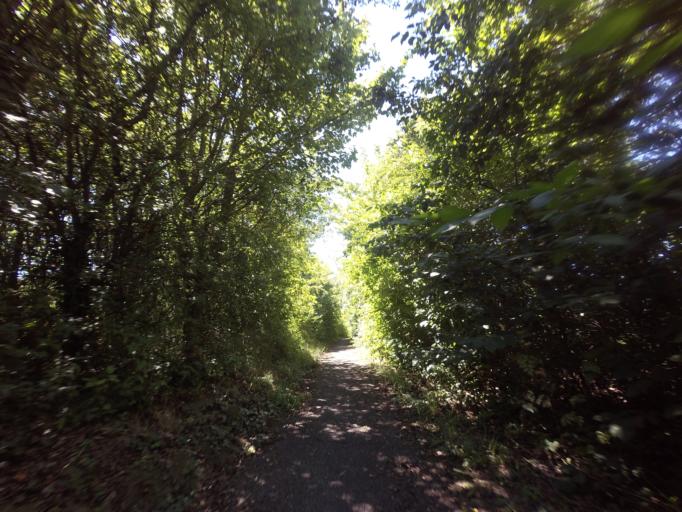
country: GB
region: England
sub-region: Kent
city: Eastry
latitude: 51.2340
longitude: 1.3075
